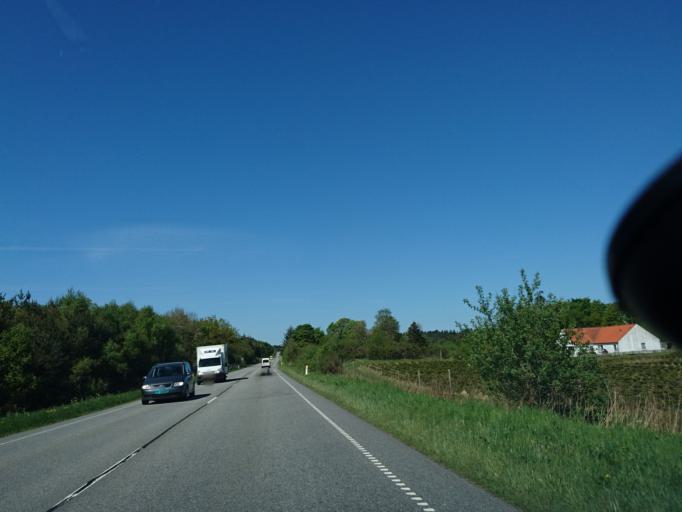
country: DK
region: North Denmark
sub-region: Hjorring Kommune
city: Sindal
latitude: 57.4577
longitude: 10.3367
